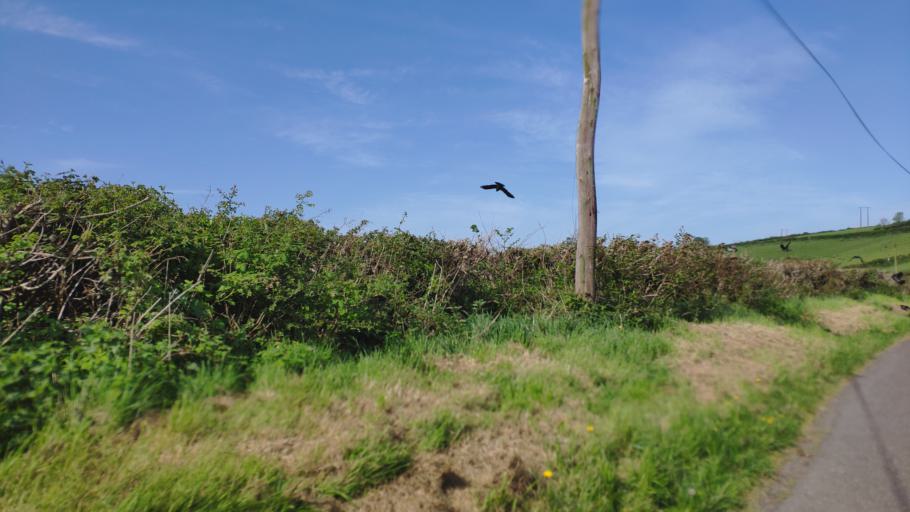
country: IE
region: Munster
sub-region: County Cork
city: Cork
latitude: 51.9174
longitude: -8.5091
